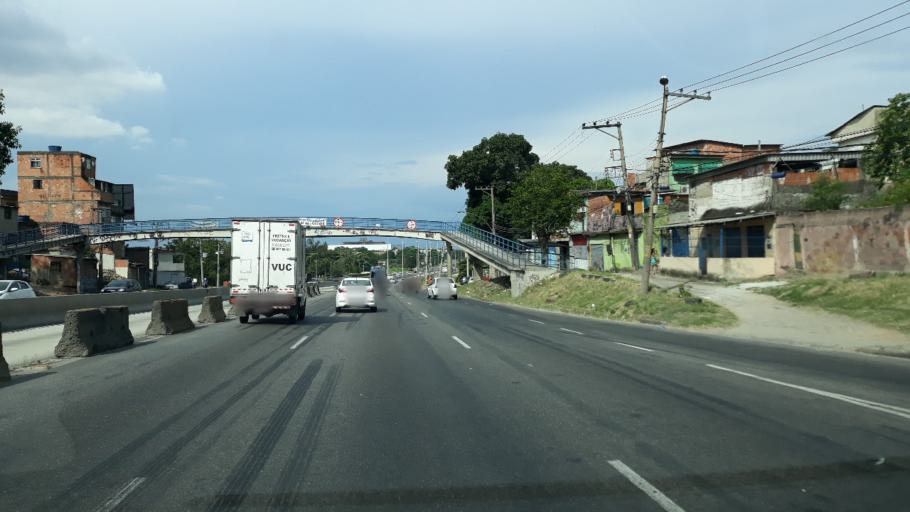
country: BR
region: Rio de Janeiro
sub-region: Sao Joao De Meriti
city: Sao Joao de Meriti
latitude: -22.8359
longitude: -43.3621
